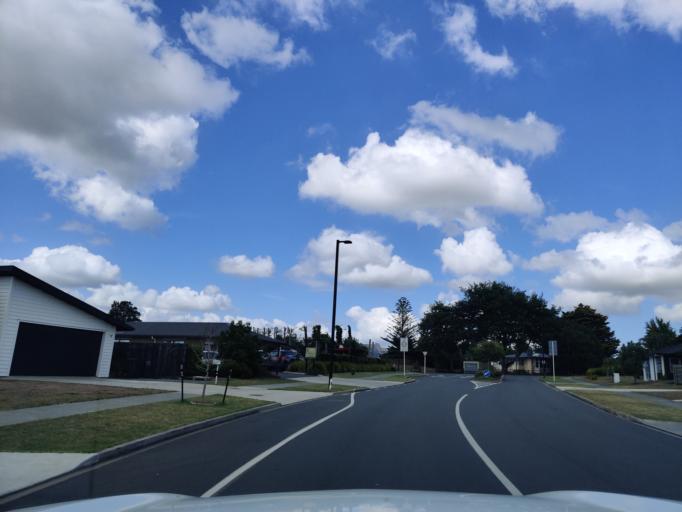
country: NZ
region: Auckland
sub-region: Auckland
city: Pukekohe East
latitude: -37.2418
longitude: 175.0160
